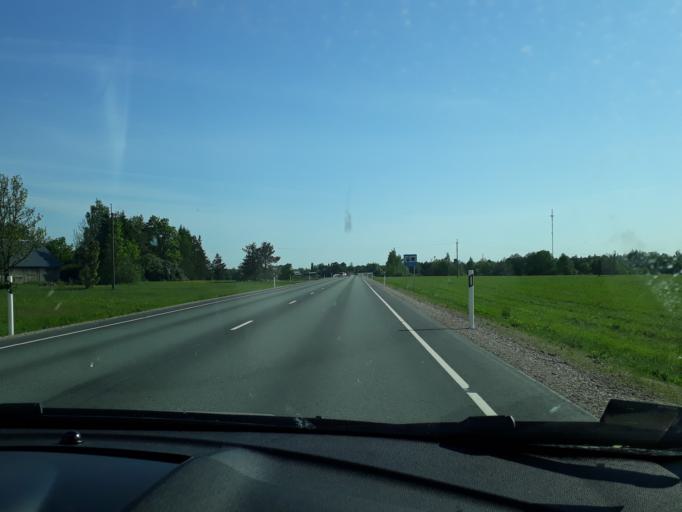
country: EE
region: Paernumaa
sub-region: Tootsi vald
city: Tootsi
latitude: 58.5276
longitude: 24.8280
